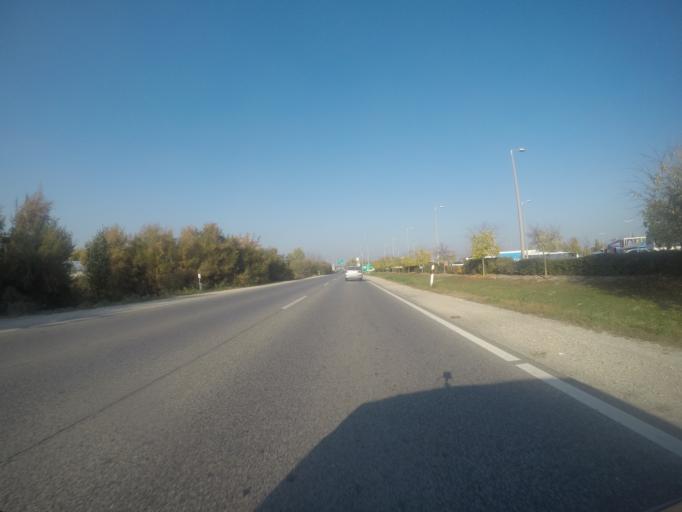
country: HU
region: Pest
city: Erd
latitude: 47.3760
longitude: 18.9347
